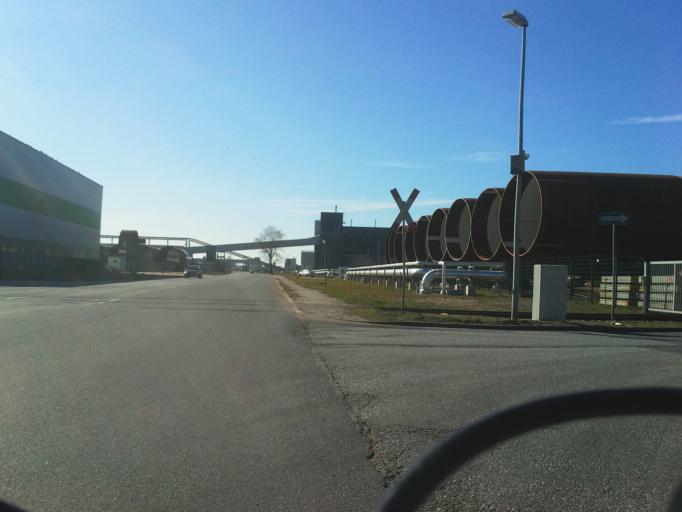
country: DE
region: Mecklenburg-Vorpommern
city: Nienhagen
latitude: 54.1490
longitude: 12.1290
